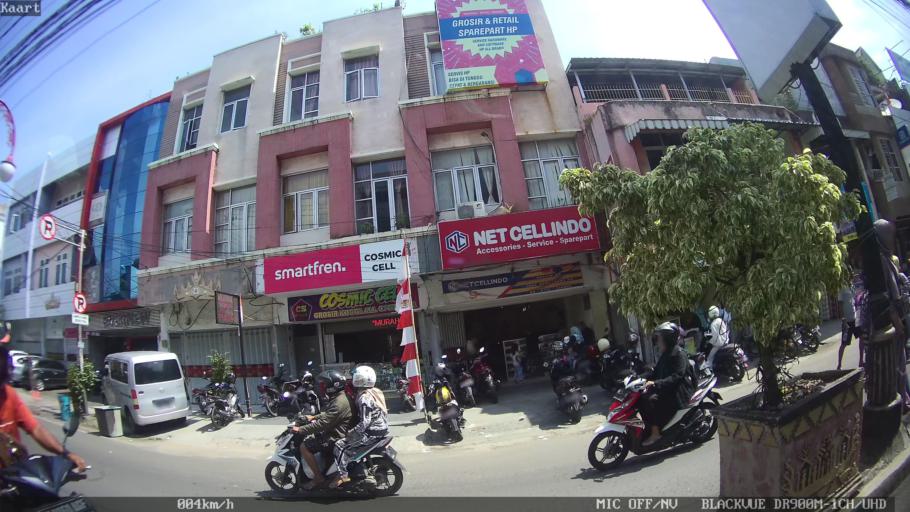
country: ID
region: Lampung
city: Bandarlampung
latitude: -5.4132
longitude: 105.2577
